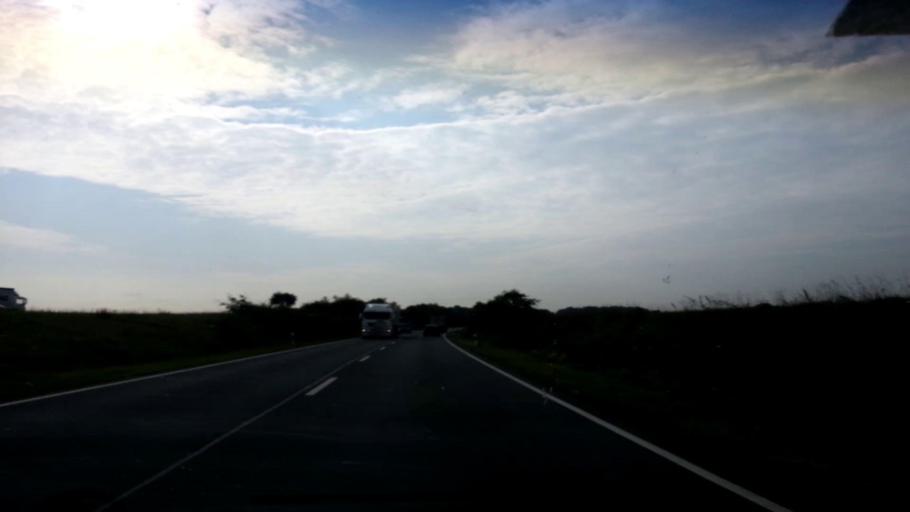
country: DE
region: Bavaria
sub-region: Regierungsbezirk Unterfranken
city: Prichsenstadt
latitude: 49.8410
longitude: 10.3522
